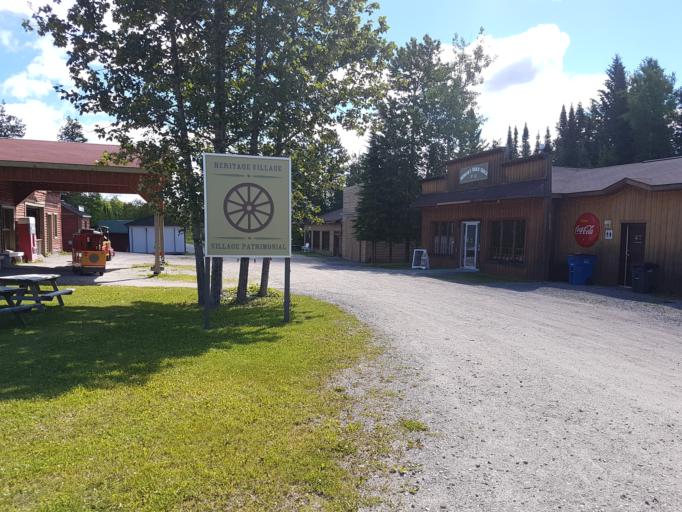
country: CA
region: Ontario
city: Iroquois Falls
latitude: 49.0521
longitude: -81.0153
